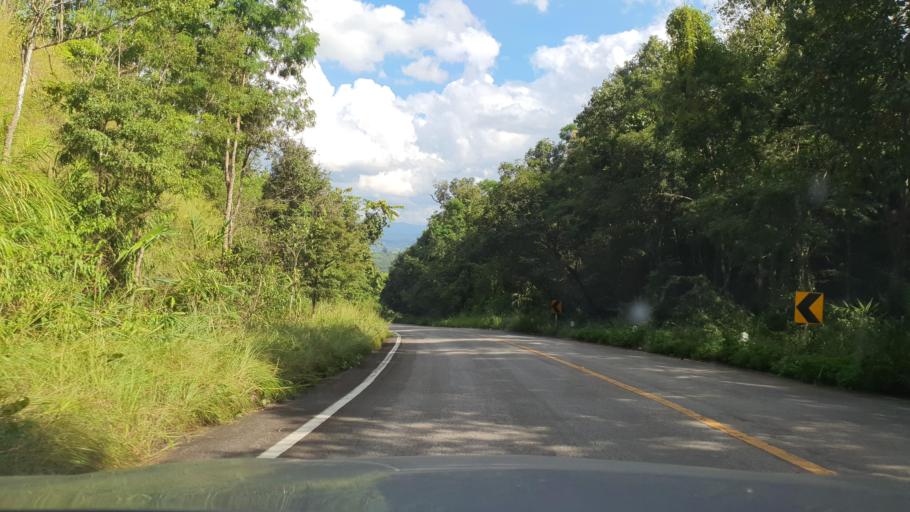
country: TH
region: Chiang Rai
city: Wiang Pa Pao
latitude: 19.3321
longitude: 99.4600
